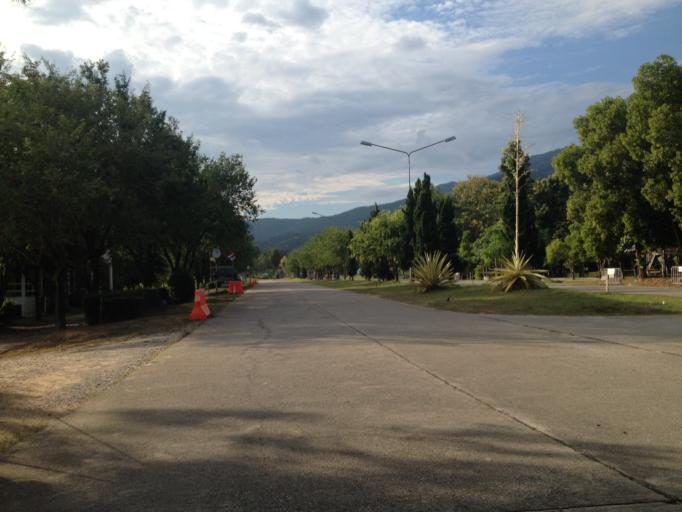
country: TH
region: Chiang Mai
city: Chiang Mai
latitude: 18.7606
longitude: 98.9365
